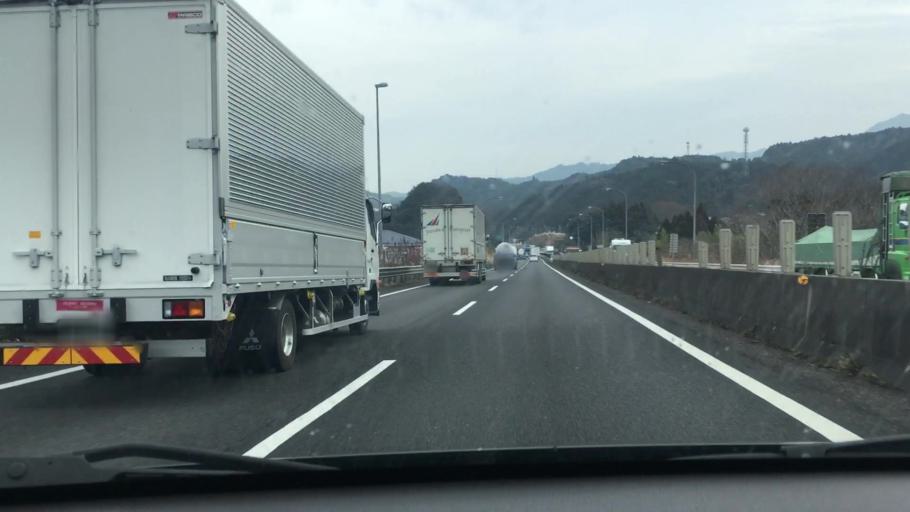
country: JP
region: Mie
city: Kameyama
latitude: 34.8357
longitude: 136.3047
